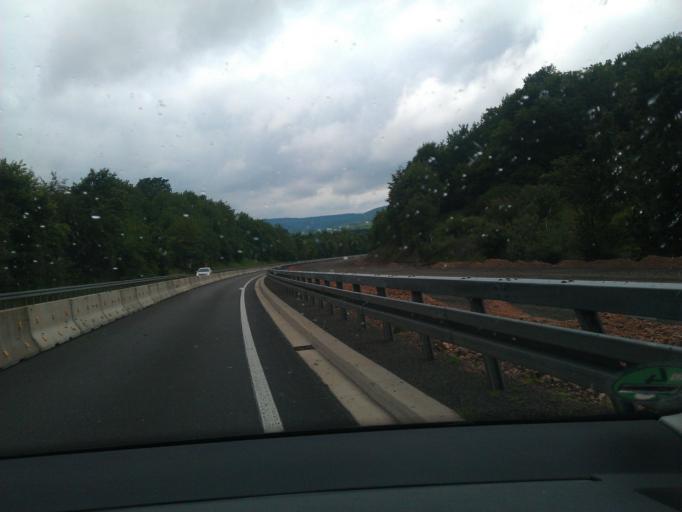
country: DE
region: Rheinland-Pfalz
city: Neuhutten
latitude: 49.5895
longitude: 7.0098
